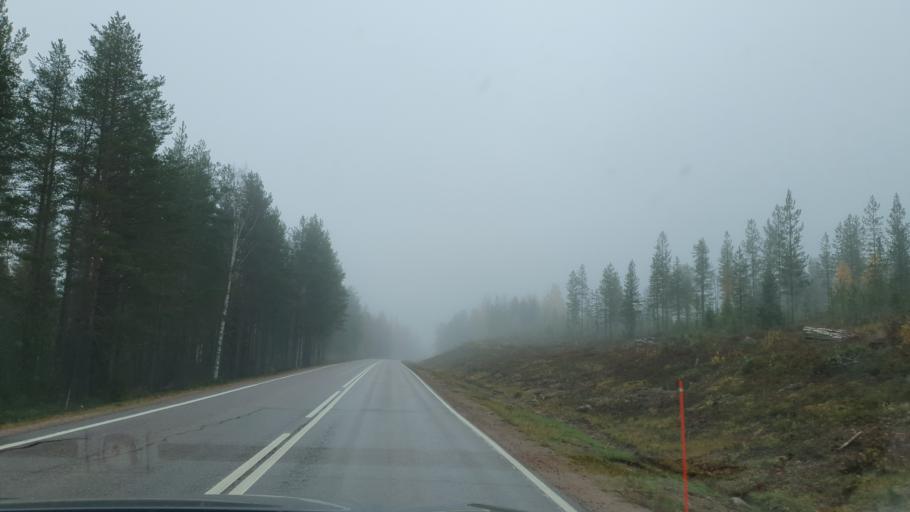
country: FI
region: Lapland
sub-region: Rovaniemi
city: Rovaniemi
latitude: 66.8126
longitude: 25.4024
